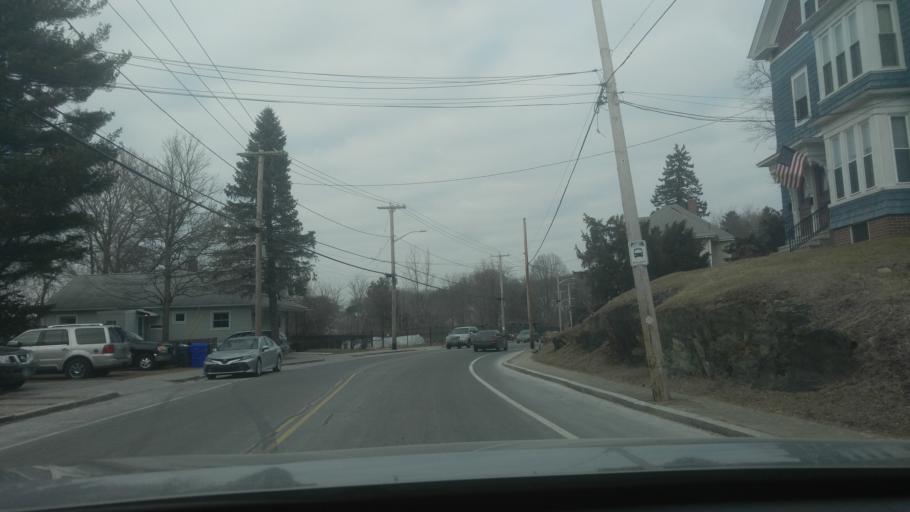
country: US
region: Rhode Island
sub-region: Providence County
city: North Providence
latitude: 41.8308
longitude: -71.4636
